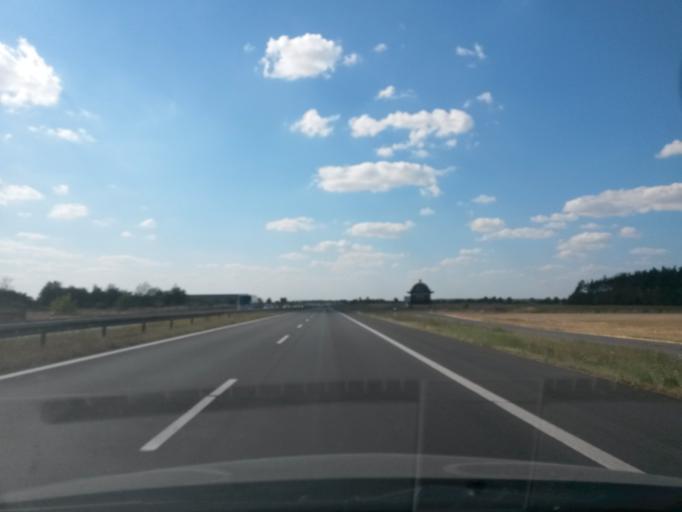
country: PL
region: Masovian Voivodeship
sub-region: Powiat nowodworski
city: Zakroczym
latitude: 52.4430
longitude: 20.6256
